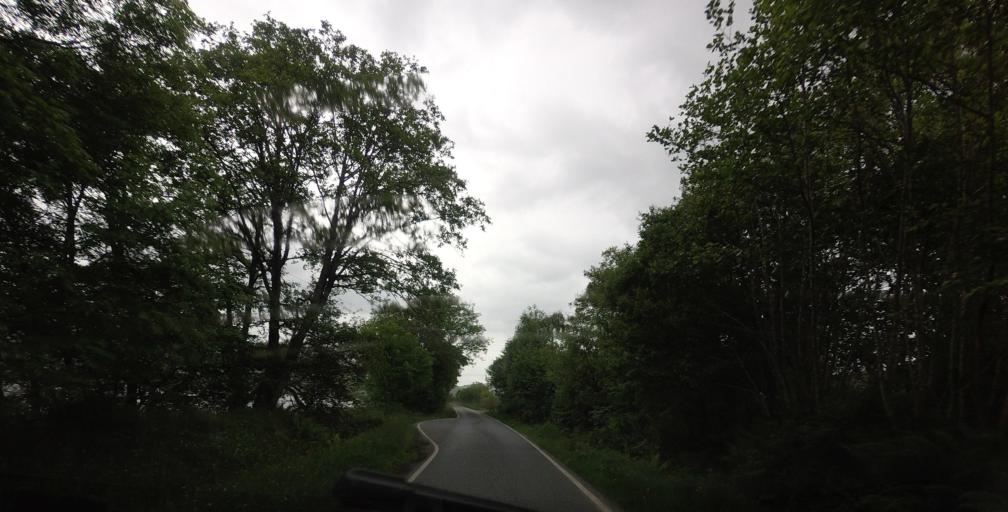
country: GB
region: Scotland
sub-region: Highland
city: Fort William
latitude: 56.8442
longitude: -5.2120
